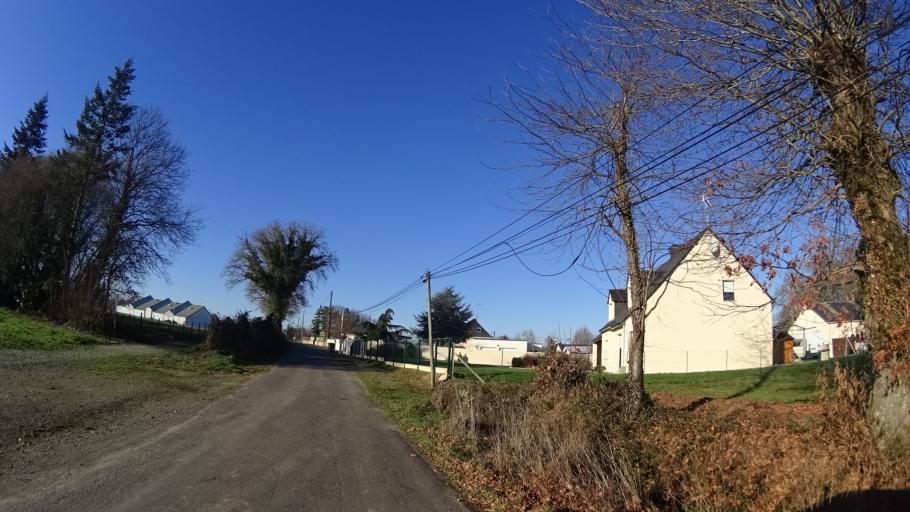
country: FR
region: Brittany
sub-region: Departement du Morbihan
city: Allaire
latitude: 47.6327
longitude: -2.1606
